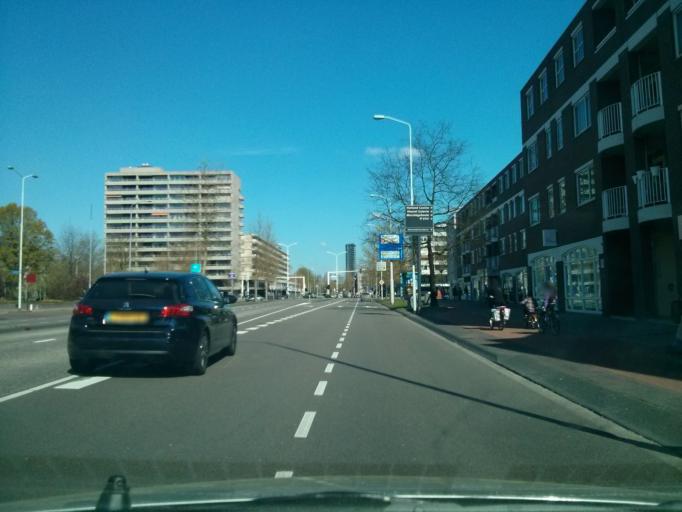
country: NL
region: North Brabant
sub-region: Gemeente Eindhoven
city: Villapark
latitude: 51.4286
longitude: 5.4870
